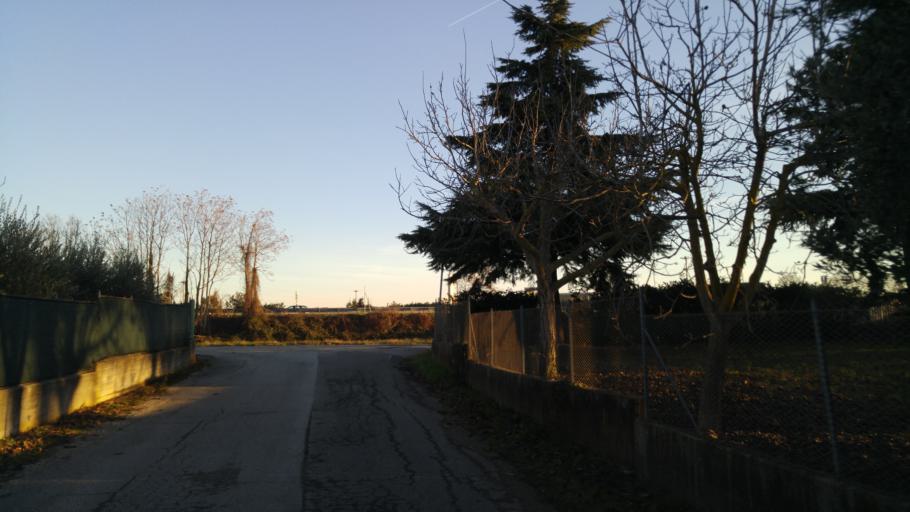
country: IT
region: The Marches
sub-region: Provincia di Pesaro e Urbino
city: Bellocchi
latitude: 43.8028
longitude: 13.0112
